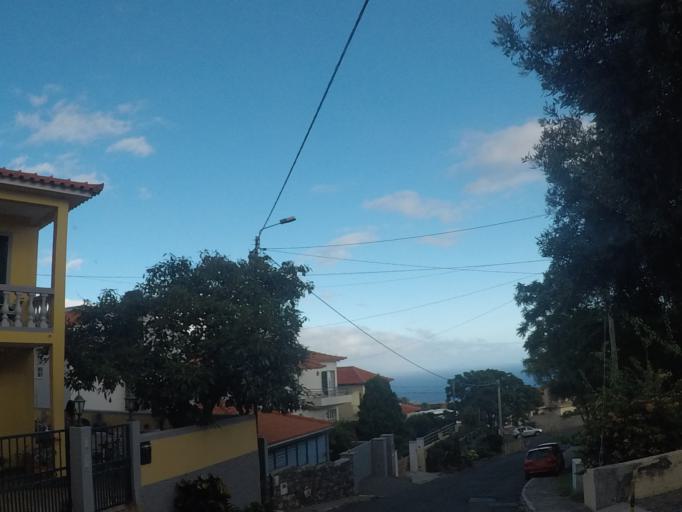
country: PT
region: Madeira
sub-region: Santa Cruz
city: Camacha
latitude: 32.6593
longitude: -16.8261
